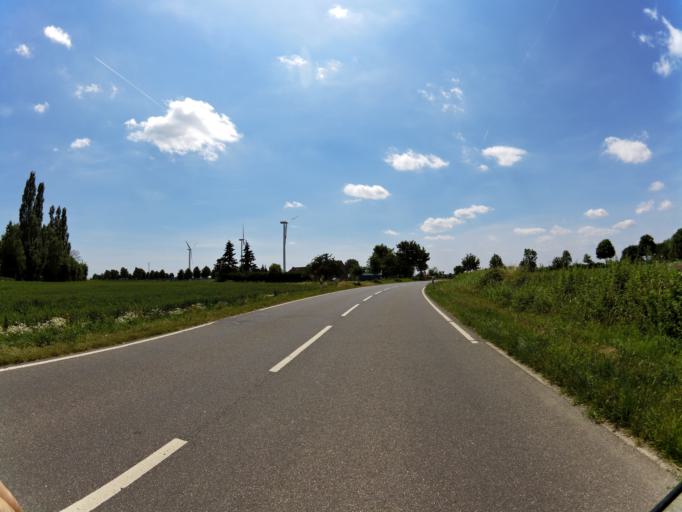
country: DE
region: North Rhine-Westphalia
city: Geilenkirchen
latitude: 51.0145
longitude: 6.1176
